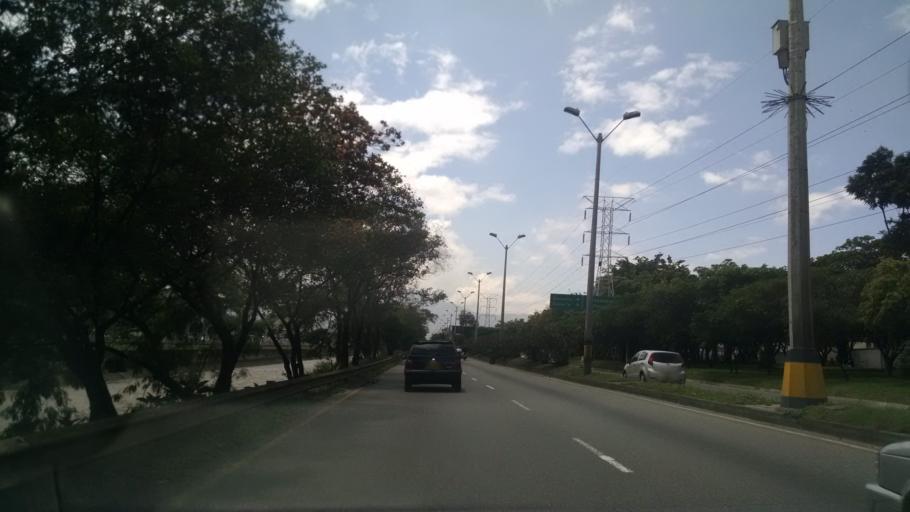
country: CO
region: Antioquia
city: Medellin
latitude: 6.2271
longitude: -75.5765
